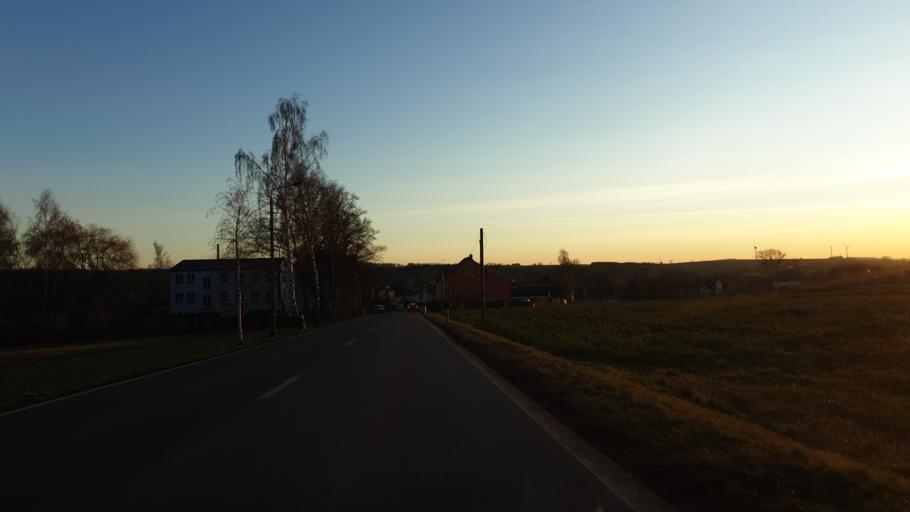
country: DE
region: Saxony
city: Kirchberg
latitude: 50.7970
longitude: 12.7562
